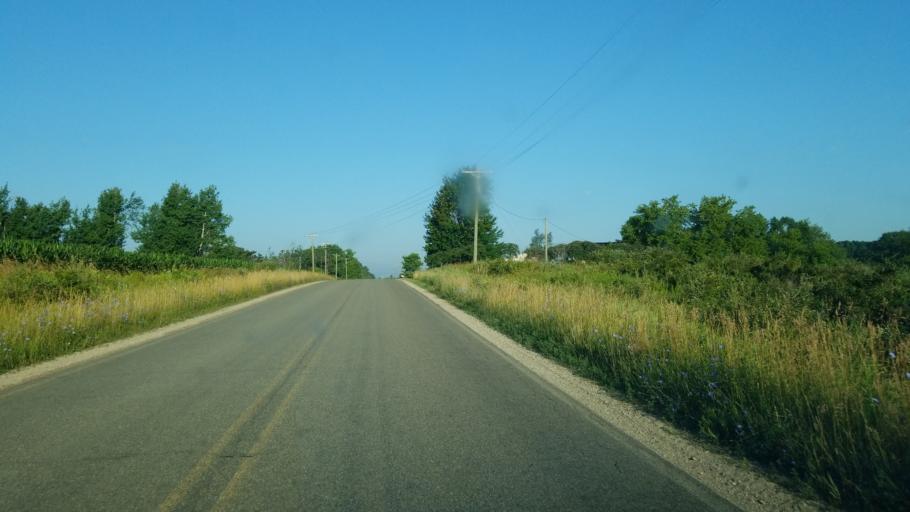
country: US
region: Michigan
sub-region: Mecosta County
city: Canadian Lakes
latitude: 43.5396
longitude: -85.1933
